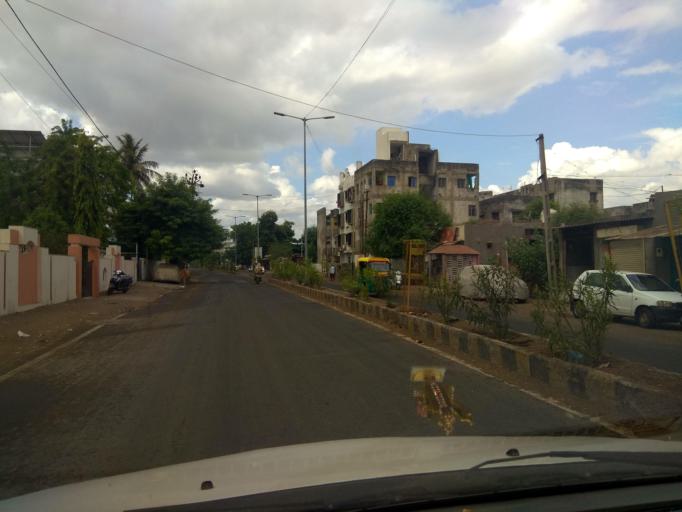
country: IN
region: Gujarat
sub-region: Bhavnagar
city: Bhavnagar
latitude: 21.7633
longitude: 72.1640
